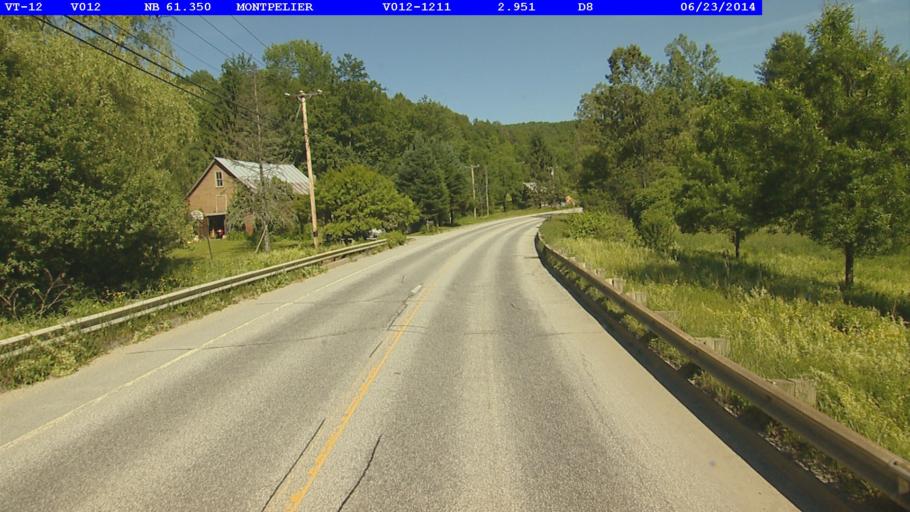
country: US
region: Vermont
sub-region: Washington County
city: Montpelier
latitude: 44.2849
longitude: -72.5762
